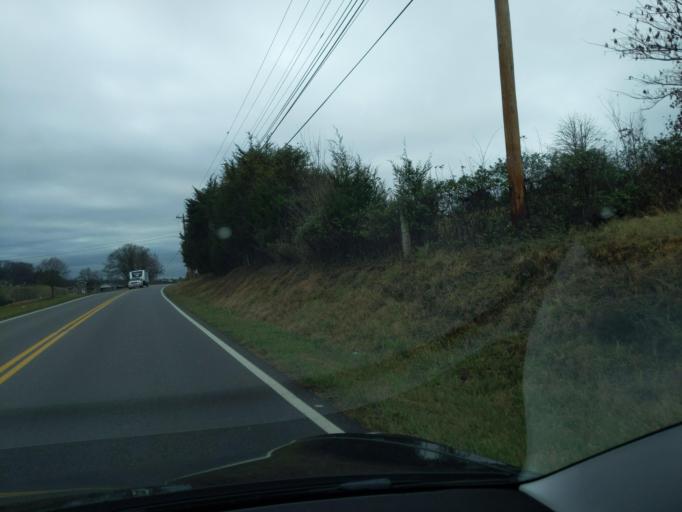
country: US
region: Tennessee
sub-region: Sevier County
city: Sevierville
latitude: 35.9652
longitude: -83.5719
